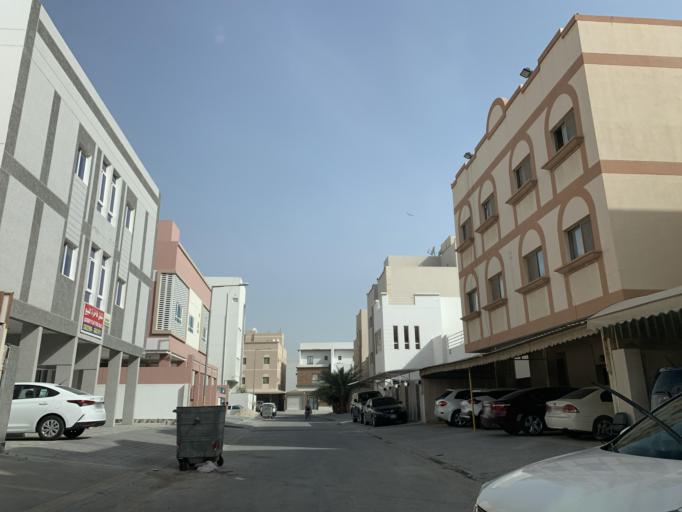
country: BH
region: Northern
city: Madinat `Isa
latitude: 26.1785
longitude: 50.5670
